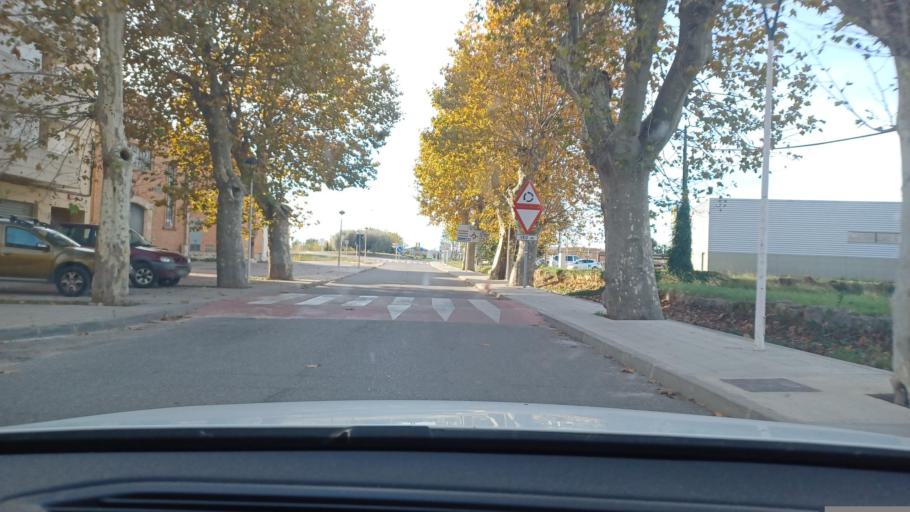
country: ES
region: Catalonia
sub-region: Provincia de Tarragona
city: Ulldecona
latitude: 40.5939
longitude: 0.4440
